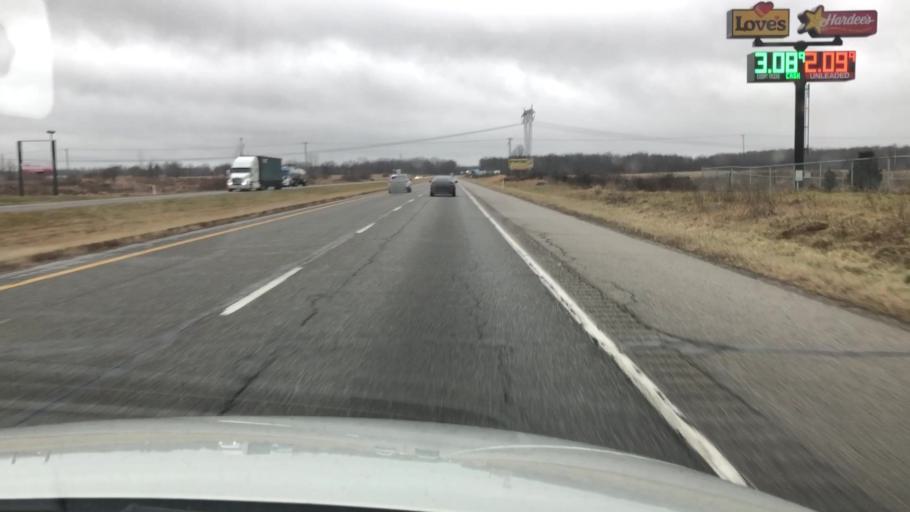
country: US
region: Indiana
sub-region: Marshall County
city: Plymouth
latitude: 41.3615
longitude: -86.3521
